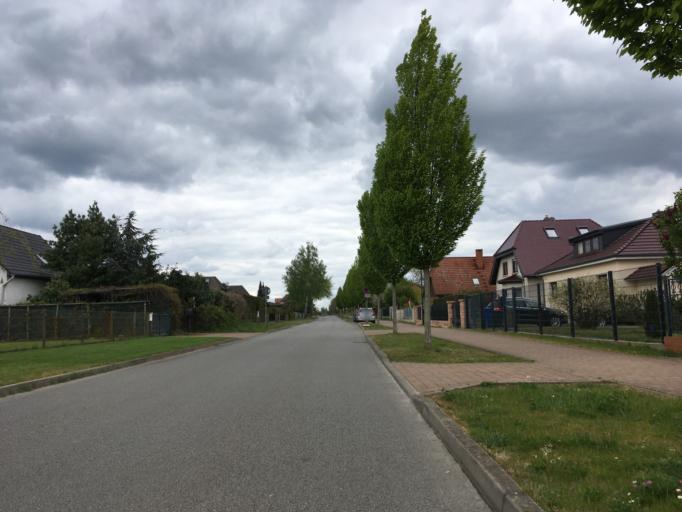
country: DE
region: Berlin
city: Buch
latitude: 52.6602
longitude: 13.5217
